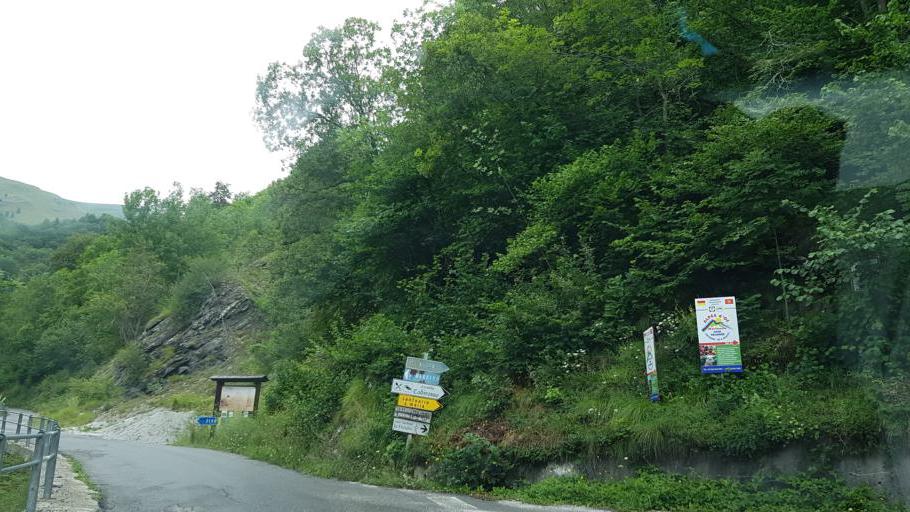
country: IT
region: Piedmont
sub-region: Provincia di Cuneo
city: Stroppo
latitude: 44.5183
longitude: 7.1288
